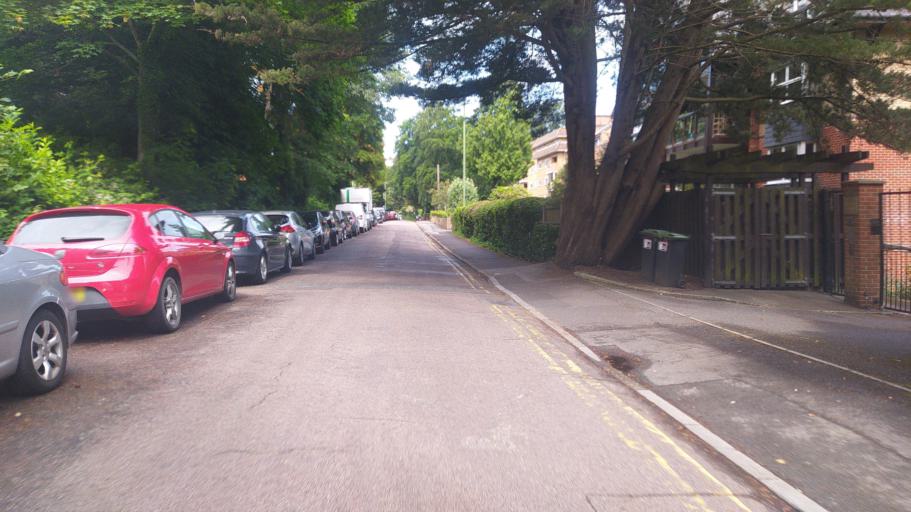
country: GB
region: England
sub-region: Bournemouth
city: Bournemouth
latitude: 50.7233
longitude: -1.8889
